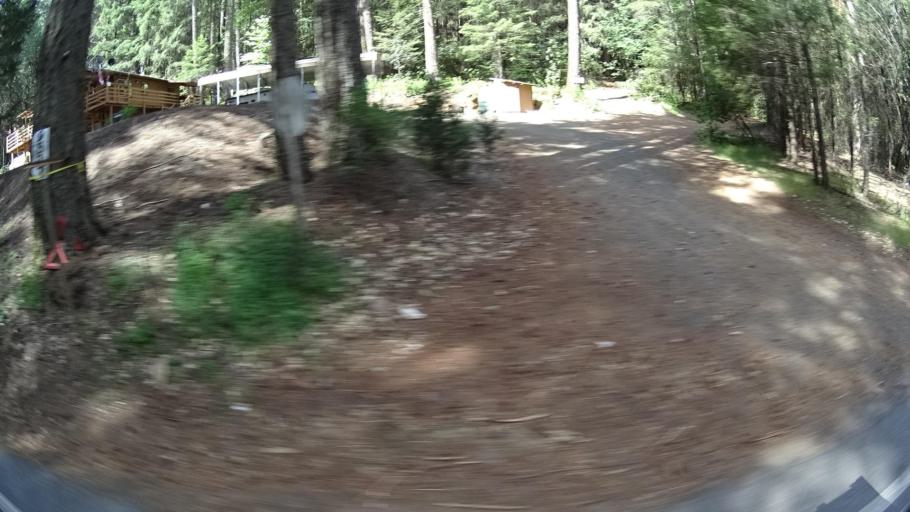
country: US
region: California
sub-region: Lake County
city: Cobb
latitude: 38.8891
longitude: -122.7319
